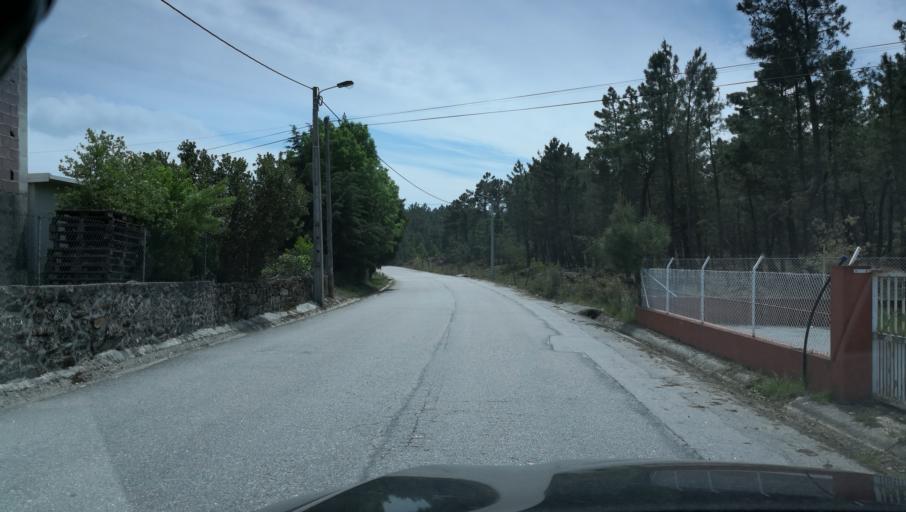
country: PT
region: Vila Real
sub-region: Vila Real
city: Vila Real
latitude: 41.2830
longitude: -7.8047
